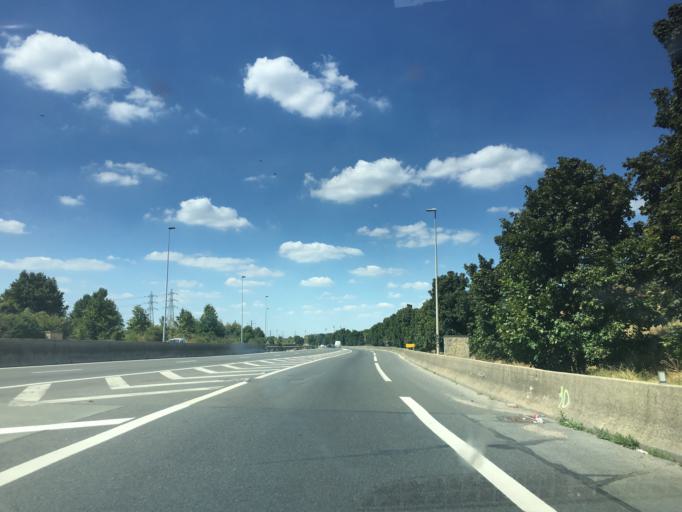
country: FR
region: Ile-de-France
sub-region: Departement du Val-de-Marne
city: Bonneuil-sur-Marne
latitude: 48.7622
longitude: 2.4676
